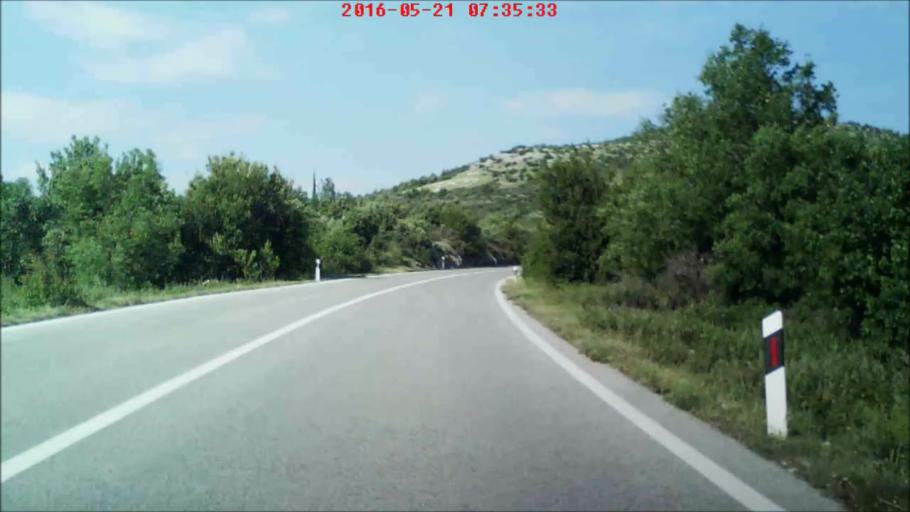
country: HR
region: Dubrovacko-Neretvanska
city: Podgora
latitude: 42.7886
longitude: 17.8779
